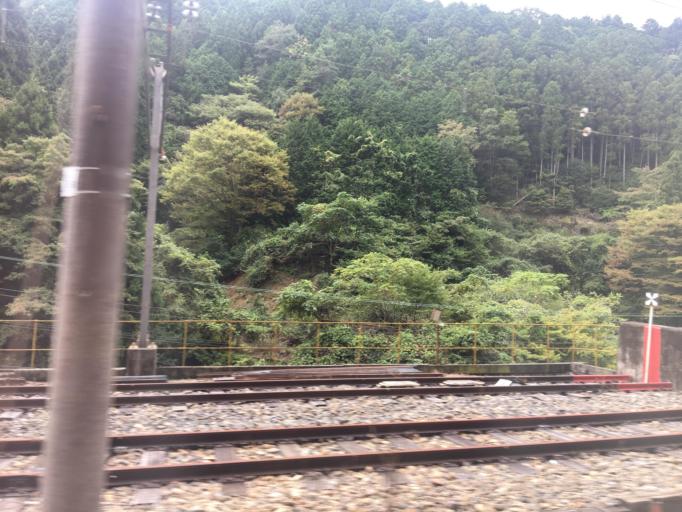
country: JP
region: Wakayama
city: Koya
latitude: 34.2353
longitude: 135.5808
